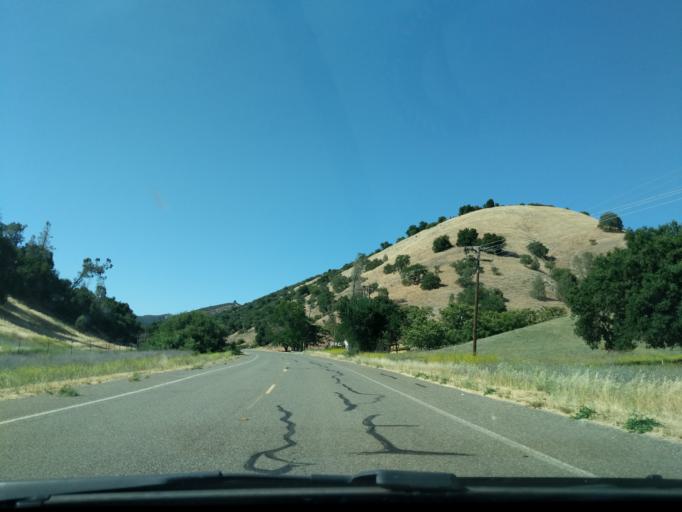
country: US
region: California
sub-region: Monterey County
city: King City
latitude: 36.0510
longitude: -121.1818
